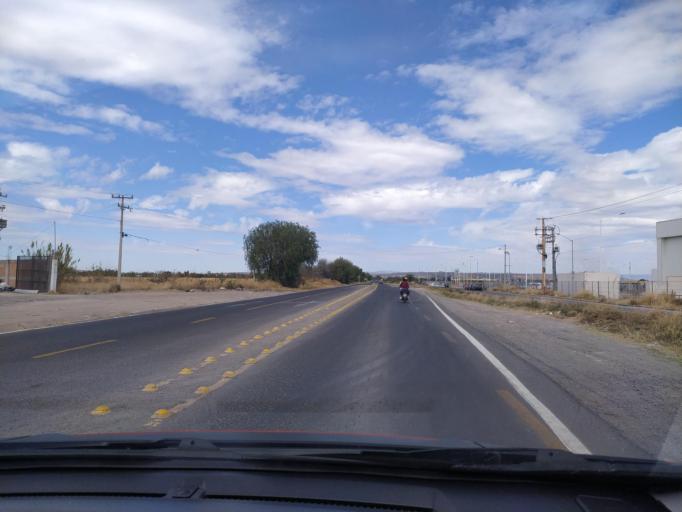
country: LA
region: Oudomxai
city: Muang La
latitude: 21.0022
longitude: 101.8317
